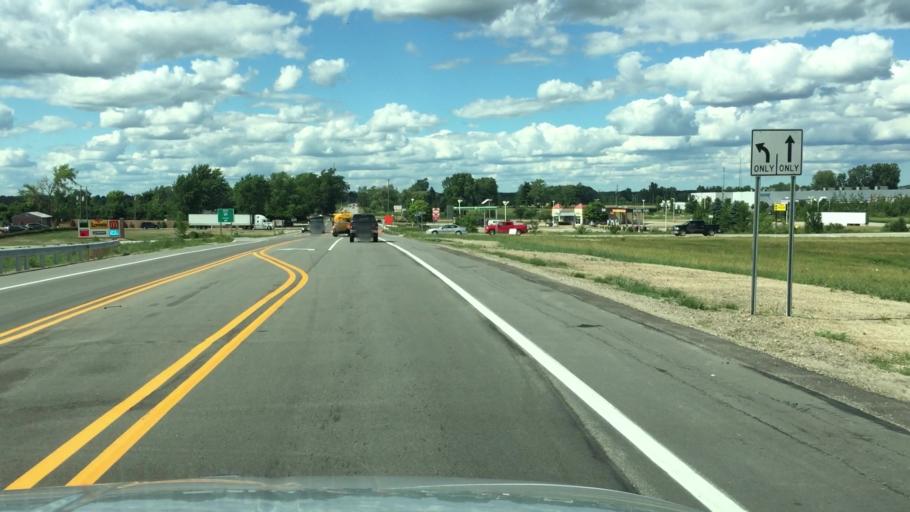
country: US
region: Michigan
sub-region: Saint Clair County
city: Capac
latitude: 42.9878
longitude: -82.9278
